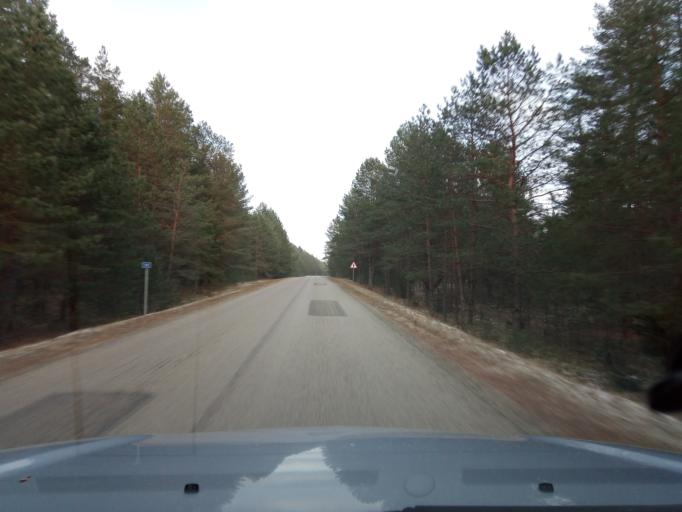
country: LT
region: Alytaus apskritis
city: Varena
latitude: 54.2052
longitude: 24.5399
